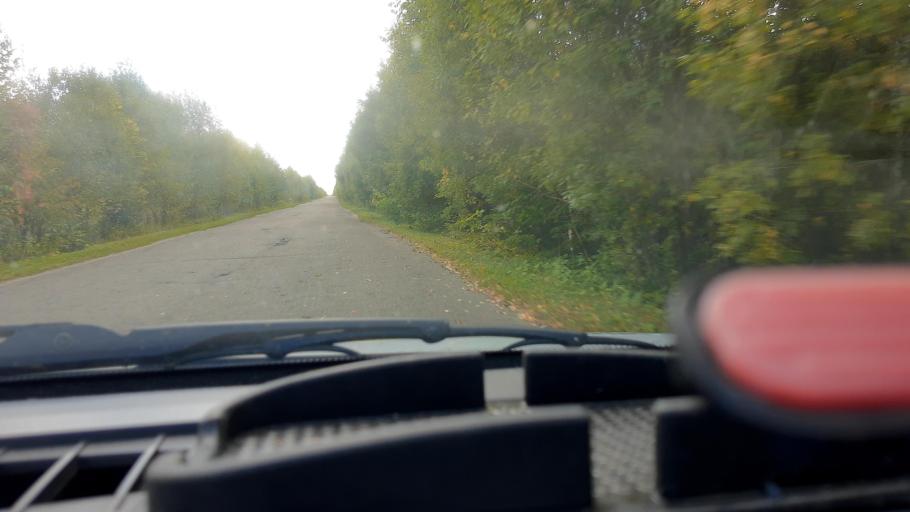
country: RU
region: Mariy-El
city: Kilemary
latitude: 56.9066
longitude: 46.7349
